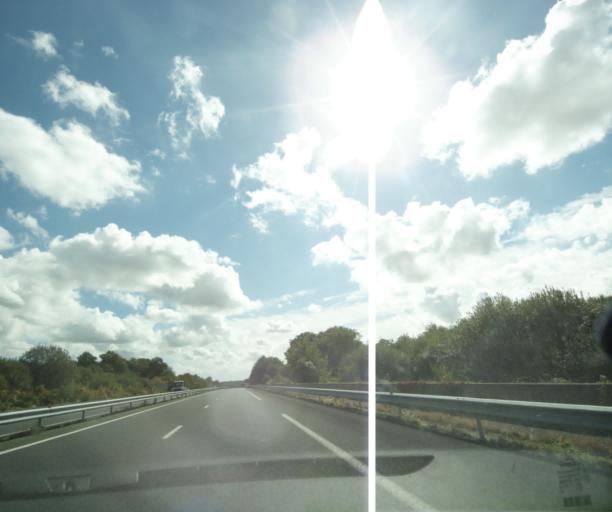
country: FR
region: Poitou-Charentes
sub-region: Departement de la Charente-Maritime
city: Saint-Georges-des-Coteaux
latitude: 45.8005
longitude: -0.6801
